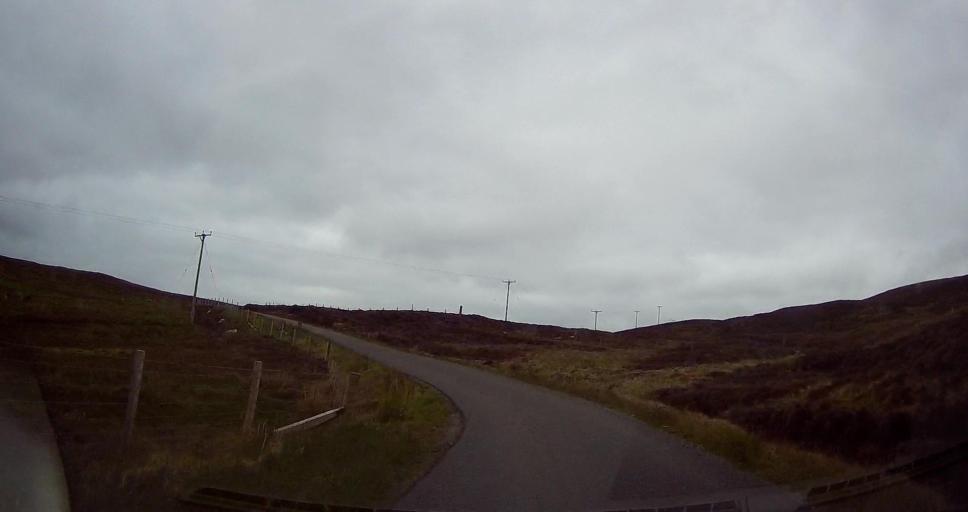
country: GB
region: Scotland
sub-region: Shetland Islands
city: Lerwick
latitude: 60.3096
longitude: -1.3374
